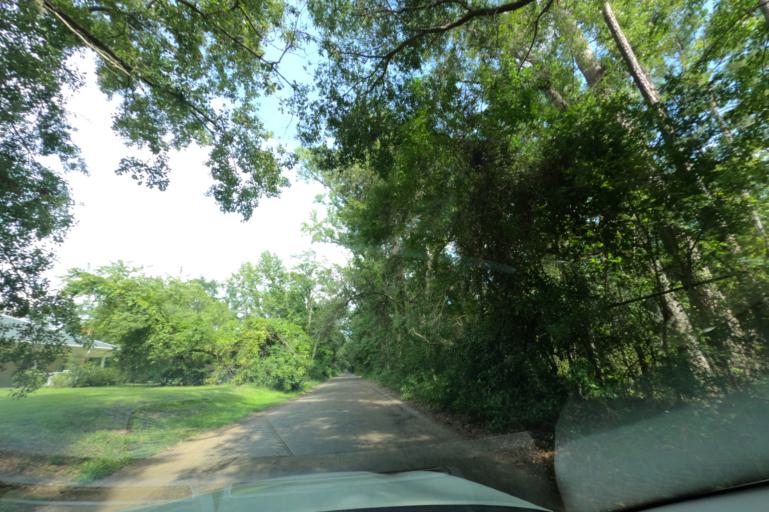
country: US
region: South Carolina
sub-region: Charleston County
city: Shell Point
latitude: 32.7168
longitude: -80.0848
